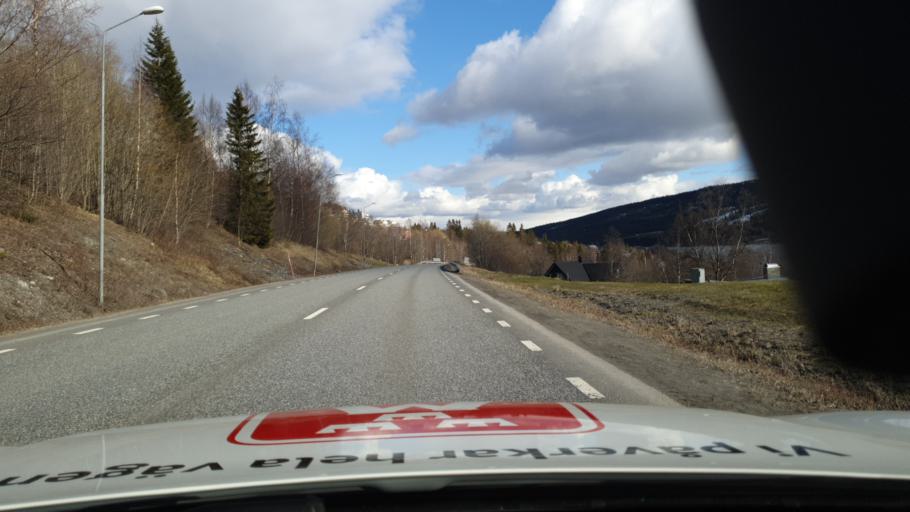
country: SE
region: Jaemtland
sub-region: Are Kommun
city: Are
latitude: 63.3982
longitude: 13.0868
